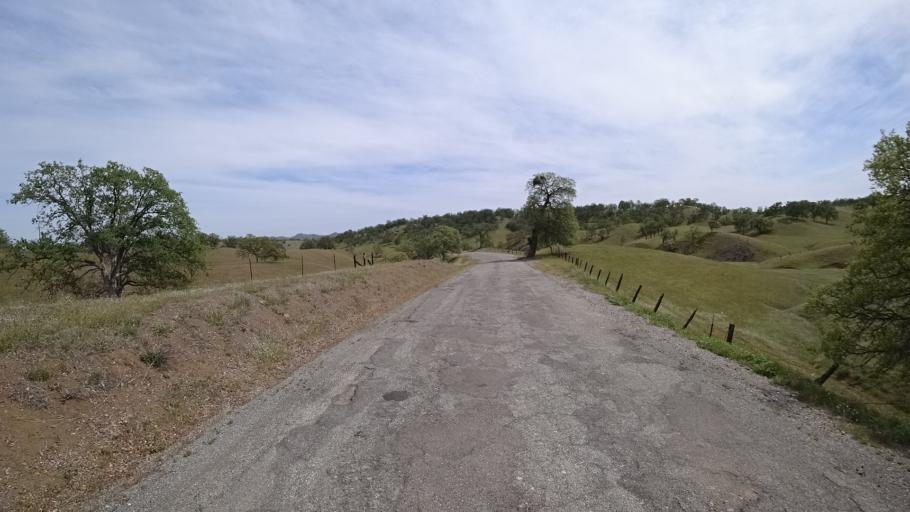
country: US
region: California
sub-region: Glenn County
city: Willows
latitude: 39.6127
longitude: -122.5785
